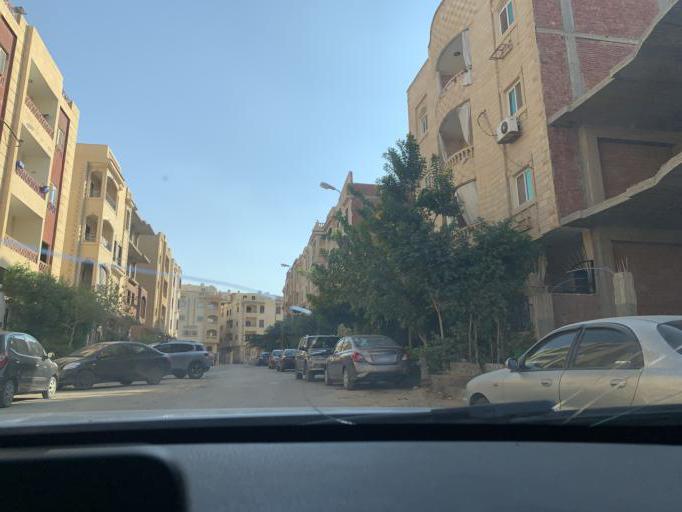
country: EG
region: Muhafazat al Qalyubiyah
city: Al Khankah
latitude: 30.0029
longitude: 31.4867
